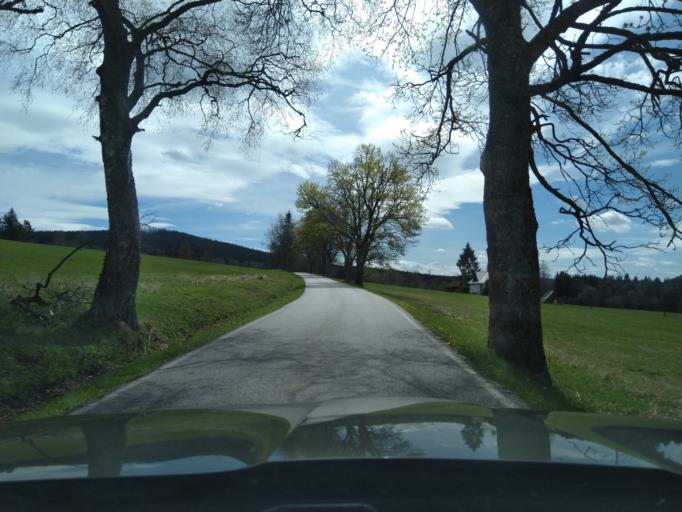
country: CZ
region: Jihocesky
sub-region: Okres Prachatice
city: Borova Lada
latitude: 49.0292
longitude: 13.6651
